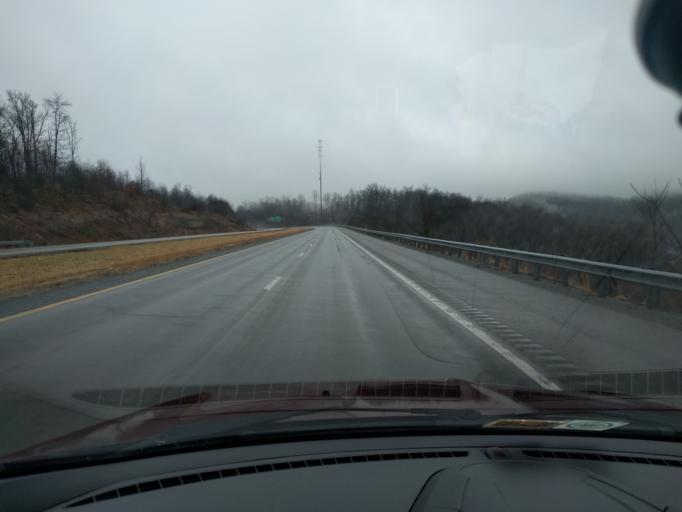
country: US
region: West Virginia
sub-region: Raleigh County
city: Sophia
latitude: 37.7144
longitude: -81.2694
